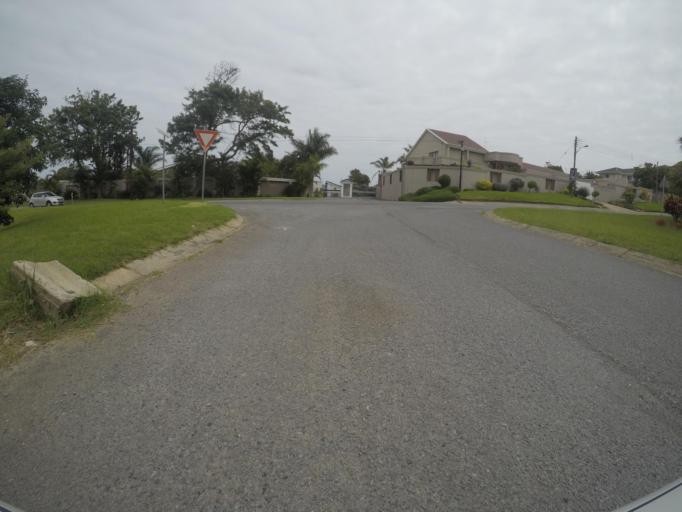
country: ZA
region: Eastern Cape
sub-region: Buffalo City Metropolitan Municipality
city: East London
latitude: -32.9787
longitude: 27.9476
